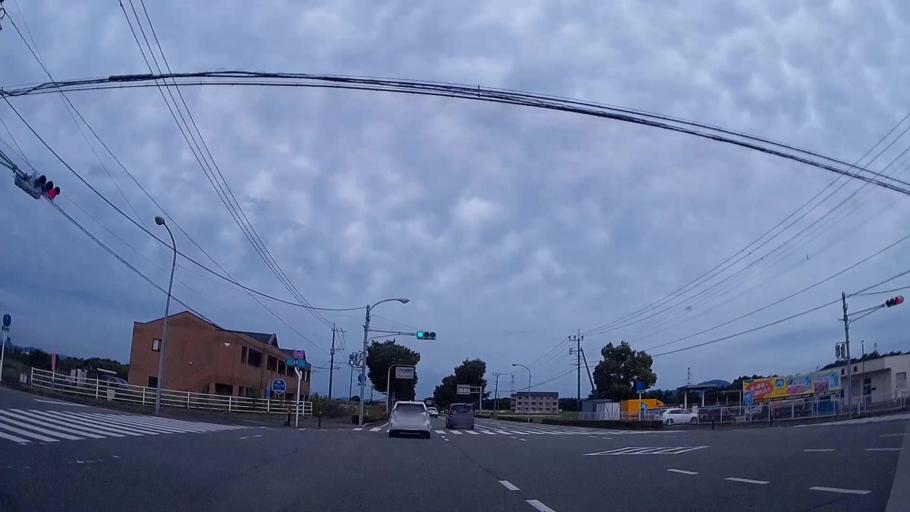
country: JP
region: Kumamoto
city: Ozu
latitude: 32.9113
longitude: 130.8440
